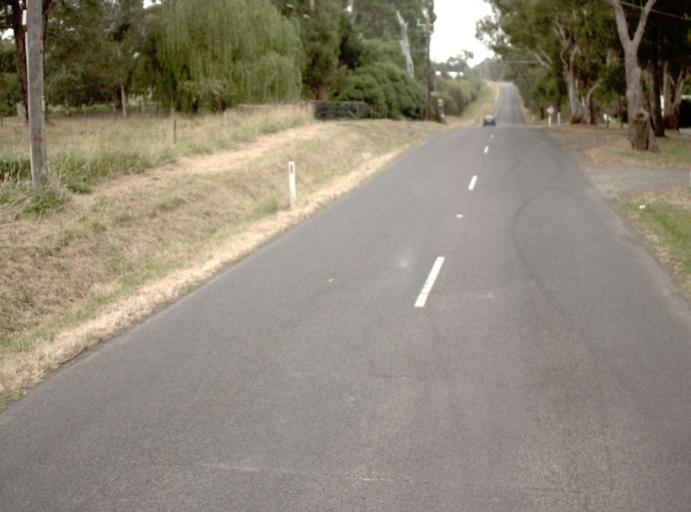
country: AU
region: Victoria
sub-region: Yarra Ranges
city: Badger Creek
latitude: -37.6861
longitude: 145.5423
